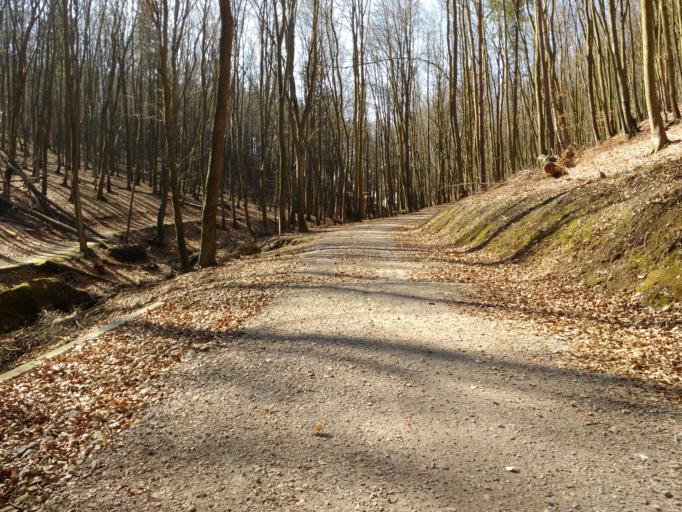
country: PL
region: Pomeranian Voivodeship
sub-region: Gdynia
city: Wielki Kack
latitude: 54.4804
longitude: 18.5150
